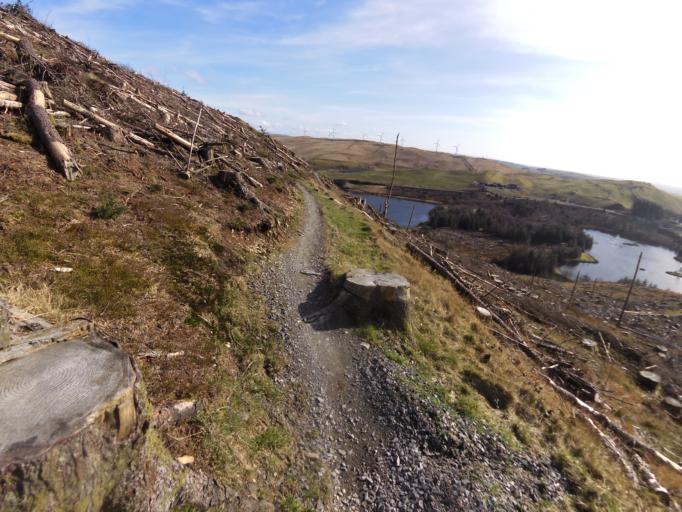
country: GB
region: Wales
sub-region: County of Ceredigion
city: Bow Street
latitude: 52.4201
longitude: -3.8807
